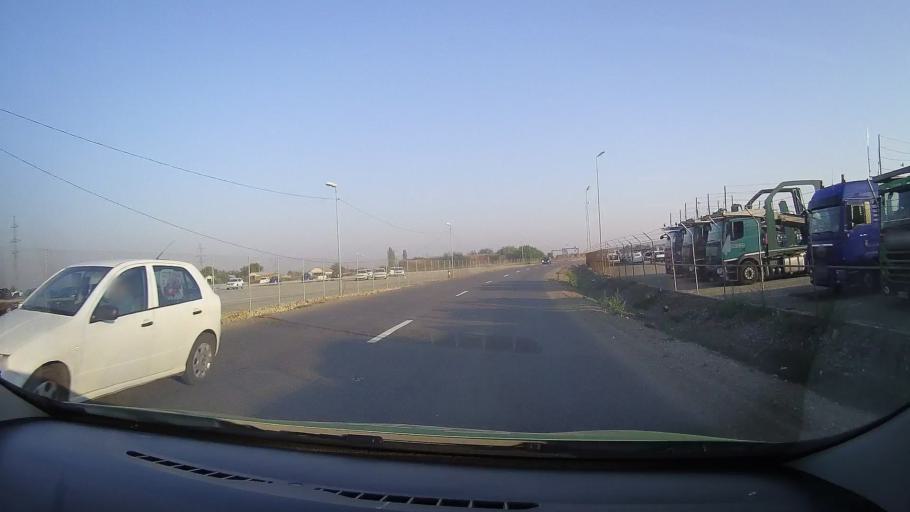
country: RO
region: Arad
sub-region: Comuna Curtici
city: Curtici
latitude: 46.3320
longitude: 21.2974
